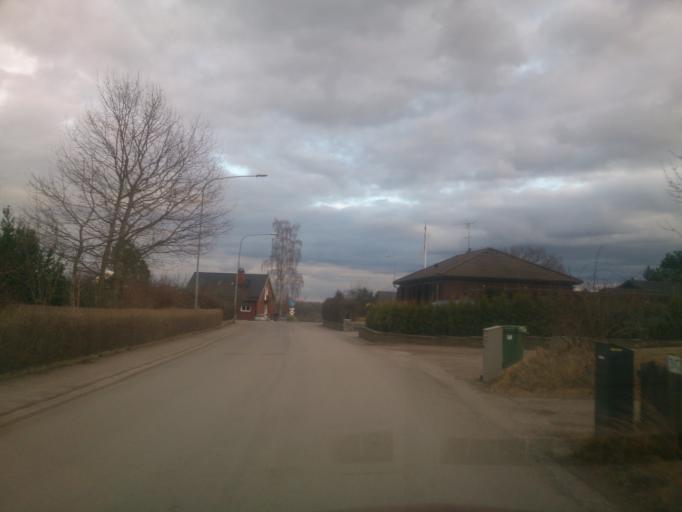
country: SE
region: OEstergoetland
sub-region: Norrkopings Kommun
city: Jursla
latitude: 58.6708
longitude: 16.1870
